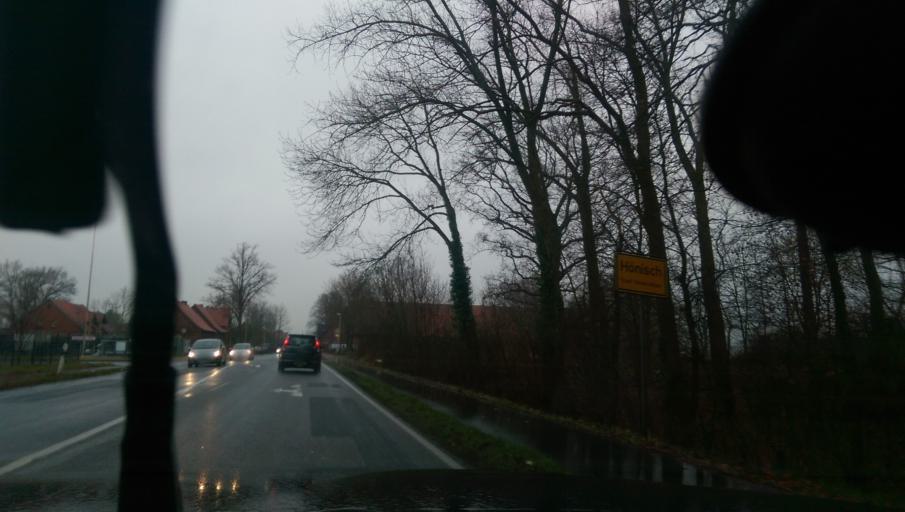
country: DE
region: Lower Saxony
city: Verden
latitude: 52.9118
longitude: 9.2171
